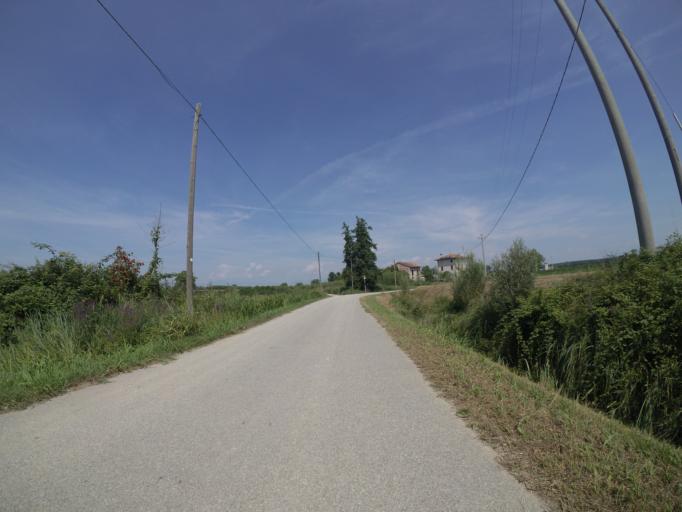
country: IT
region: Friuli Venezia Giulia
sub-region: Provincia di Udine
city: Varmo
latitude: 45.9030
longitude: 12.9787
